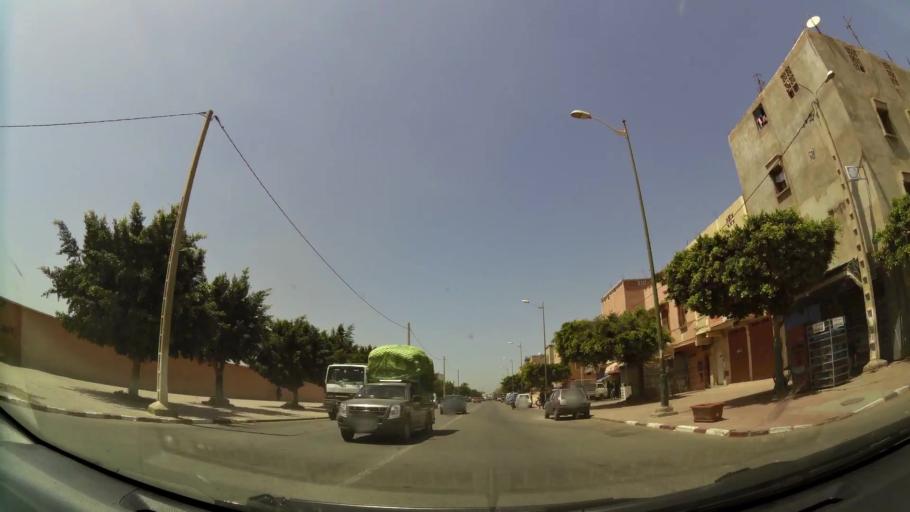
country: MA
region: Souss-Massa-Draa
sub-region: Inezgane-Ait Mellou
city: Inezgane
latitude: 30.3413
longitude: -9.4854
